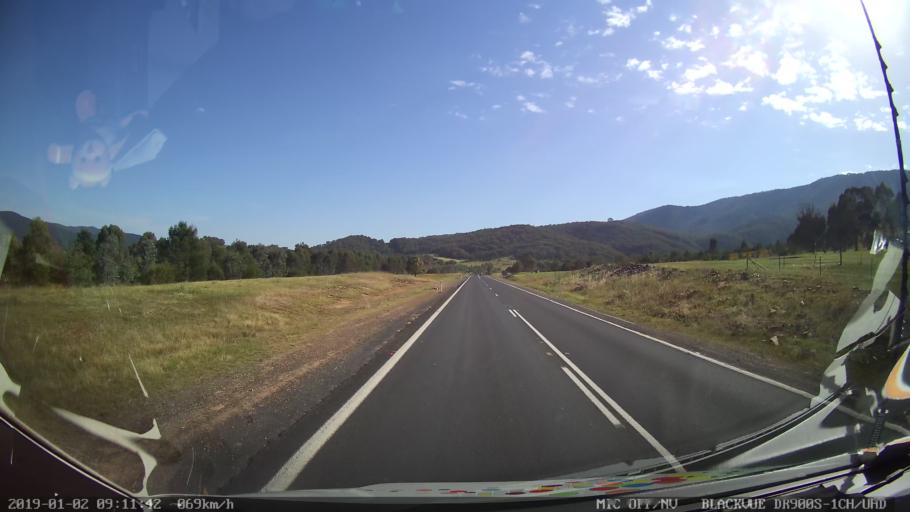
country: AU
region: New South Wales
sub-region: Tumut Shire
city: Tumut
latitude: -35.5090
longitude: 148.2701
